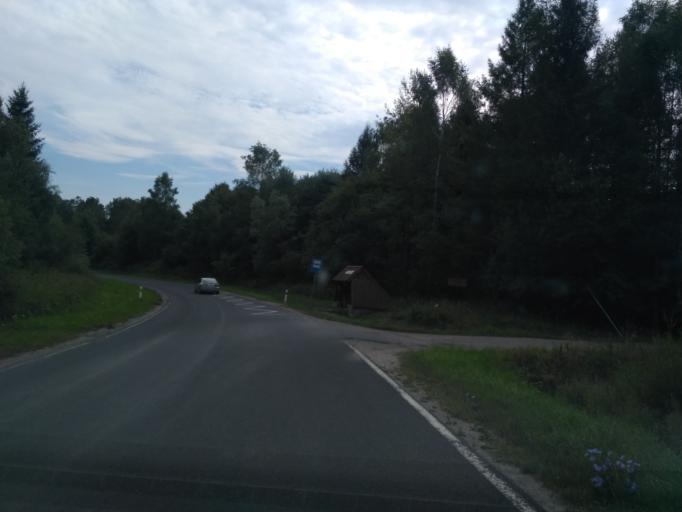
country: PL
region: Subcarpathian Voivodeship
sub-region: Powiat bieszczadzki
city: Lutowiska
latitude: 49.1997
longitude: 22.6749
